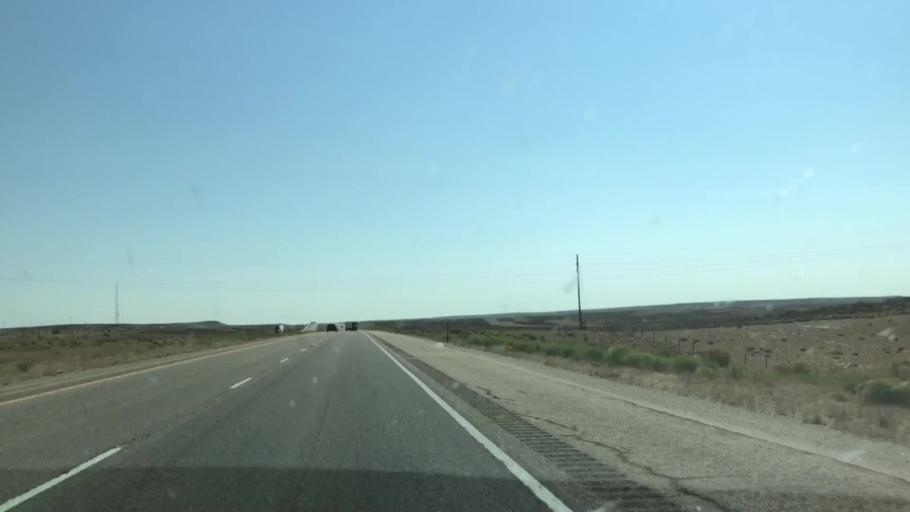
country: US
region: Wyoming
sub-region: Sweetwater County
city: Rock Springs
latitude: 41.6322
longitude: -108.3630
